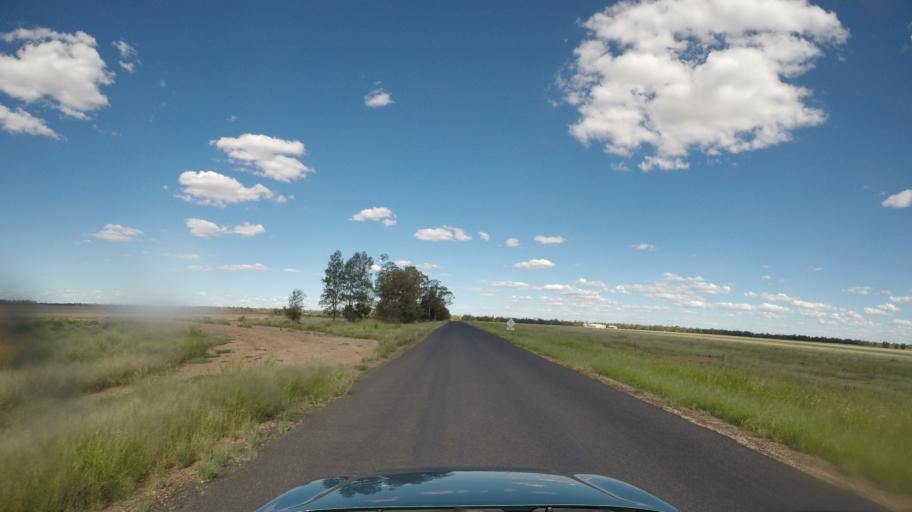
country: AU
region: Queensland
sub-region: Goondiwindi
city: Goondiwindi
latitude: -28.1780
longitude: 150.2723
